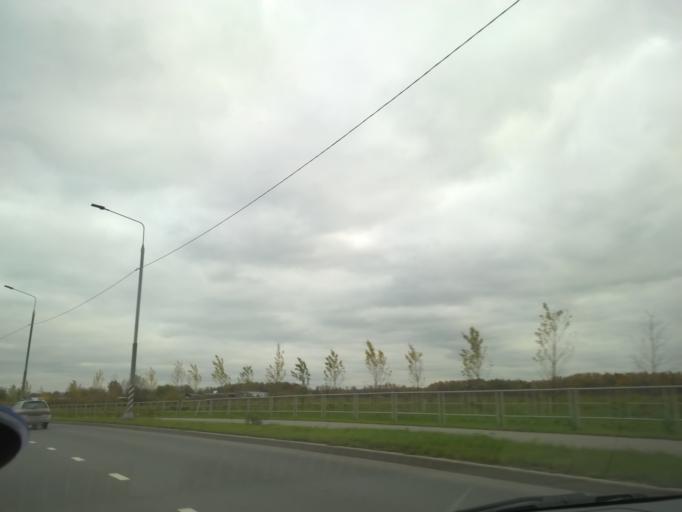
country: RU
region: Moskovskaya
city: Kommunarka
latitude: 55.5551
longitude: 37.4914
